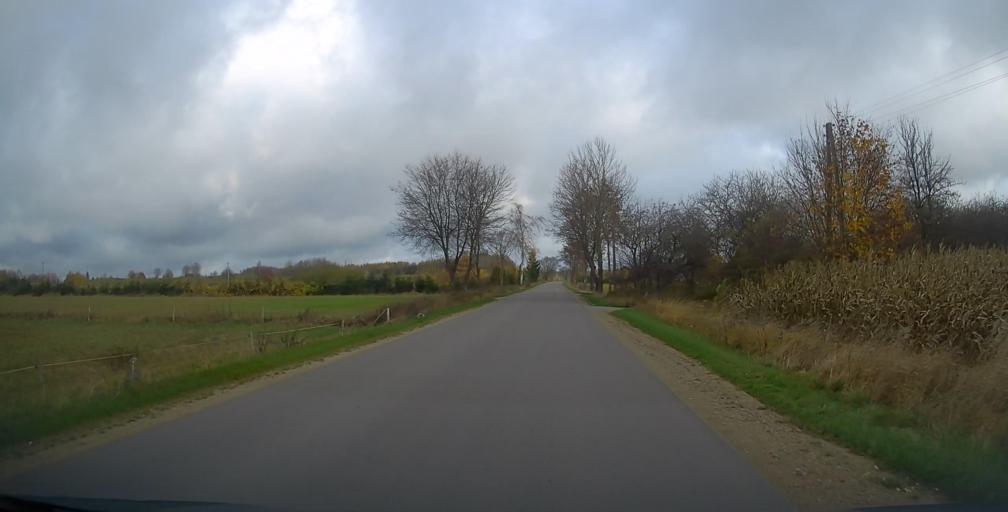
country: PL
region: Podlasie
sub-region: Suwalki
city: Suwalki
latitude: 54.2925
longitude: 22.8787
